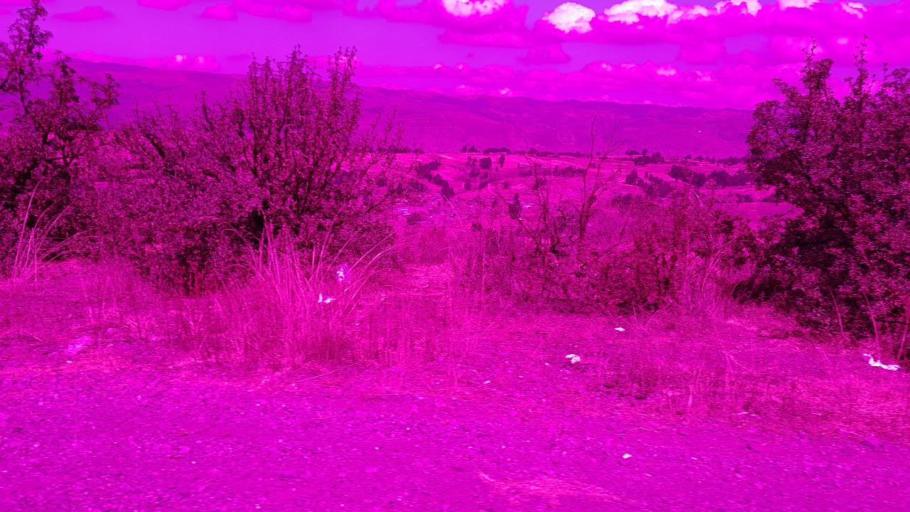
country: PE
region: Cusco
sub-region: Provincia de Cusco
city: Cusco
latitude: -13.4971
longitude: -71.9262
